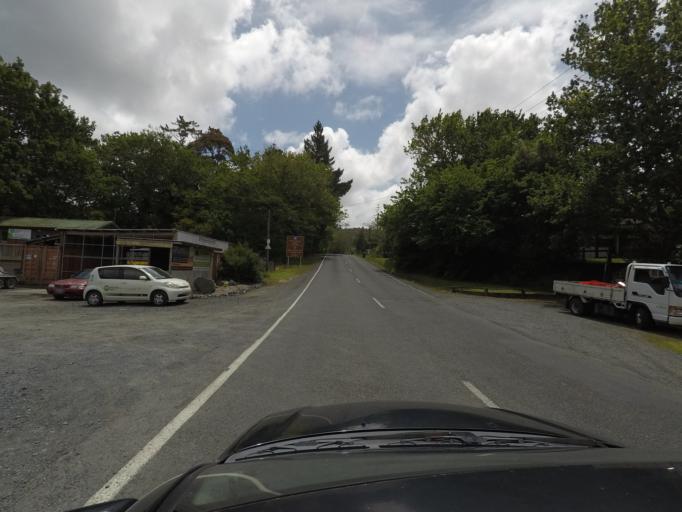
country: NZ
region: Auckland
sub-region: Auckland
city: Warkworth
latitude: -36.5116
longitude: 174.6609
